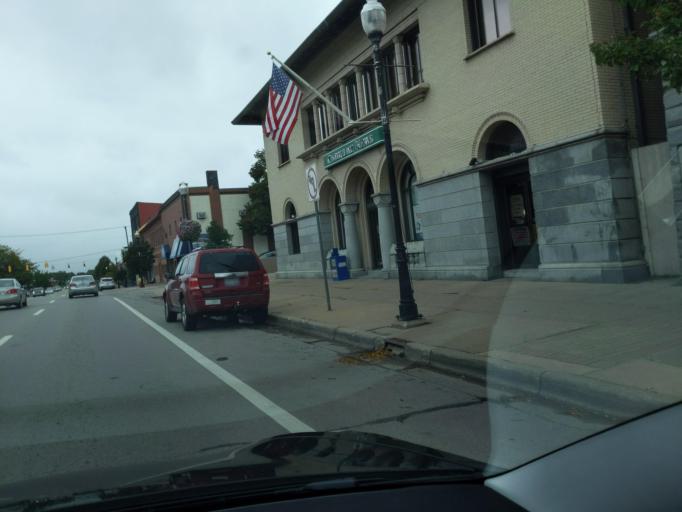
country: US
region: Michigan
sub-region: Wexford County
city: Cadillac
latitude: 44.2511
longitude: -85.4000
